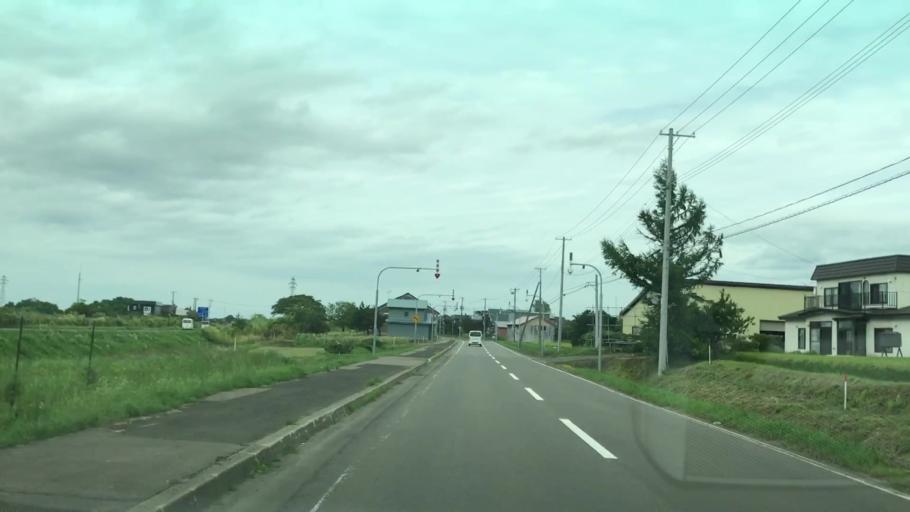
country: JP
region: Hokkaido
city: Iwanai
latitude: 42.9831
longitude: 140.6174
